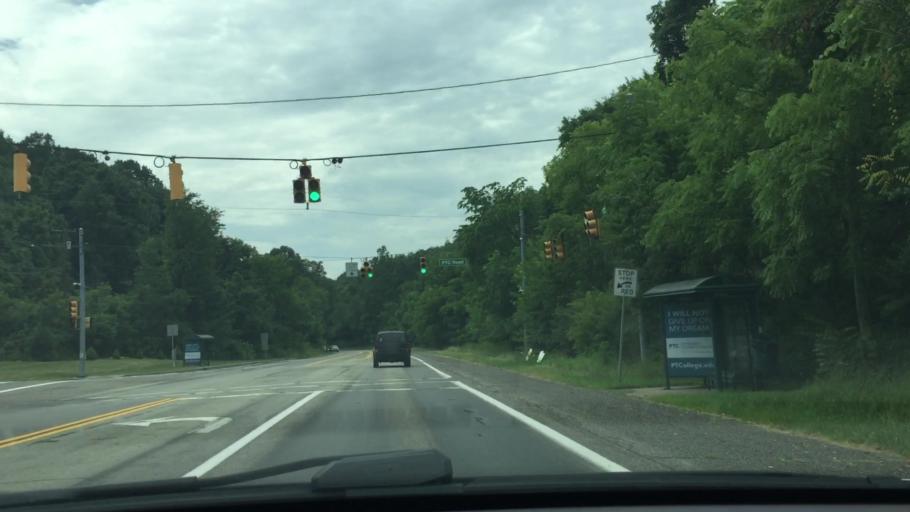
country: US
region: Pennsylvania
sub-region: Allegheny County
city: Oakdale
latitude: 40.4223
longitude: -80.1920
